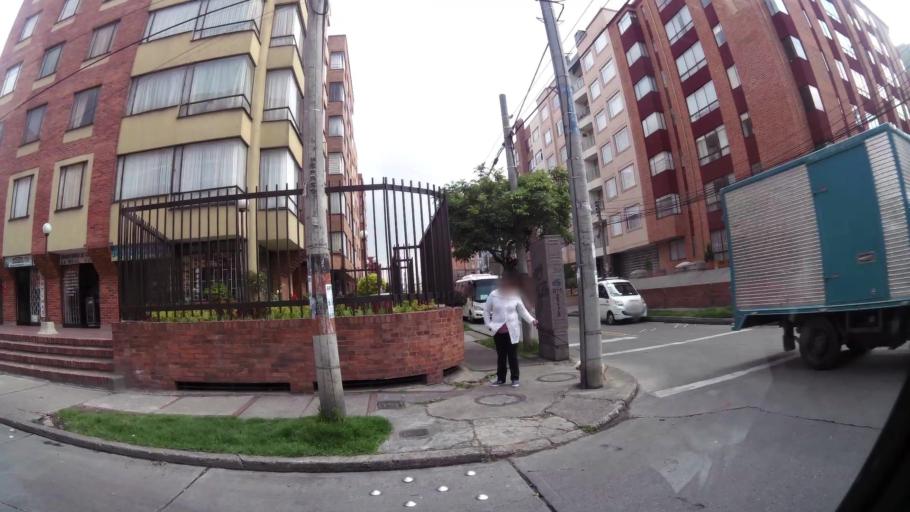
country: CO
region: Bogota D.C.
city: Barrio San Luis
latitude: 4.7333
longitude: -74.0527
